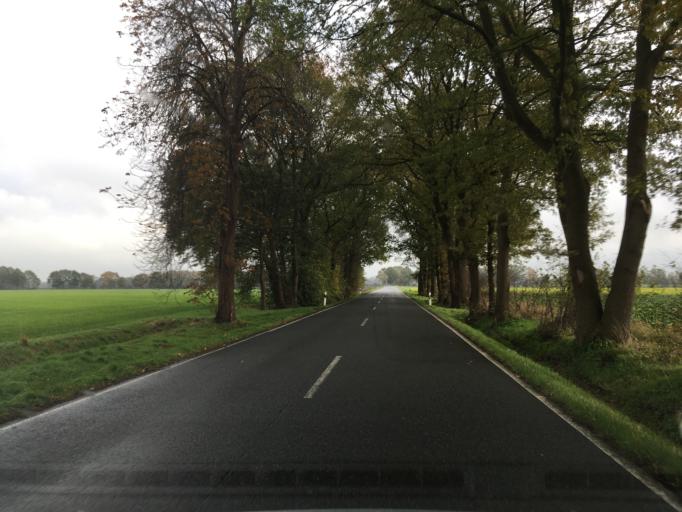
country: DE
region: North Rhine-Westphalia
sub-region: Regierungsbezirk Munster
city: Velen
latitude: 51.8712
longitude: 7.0229
